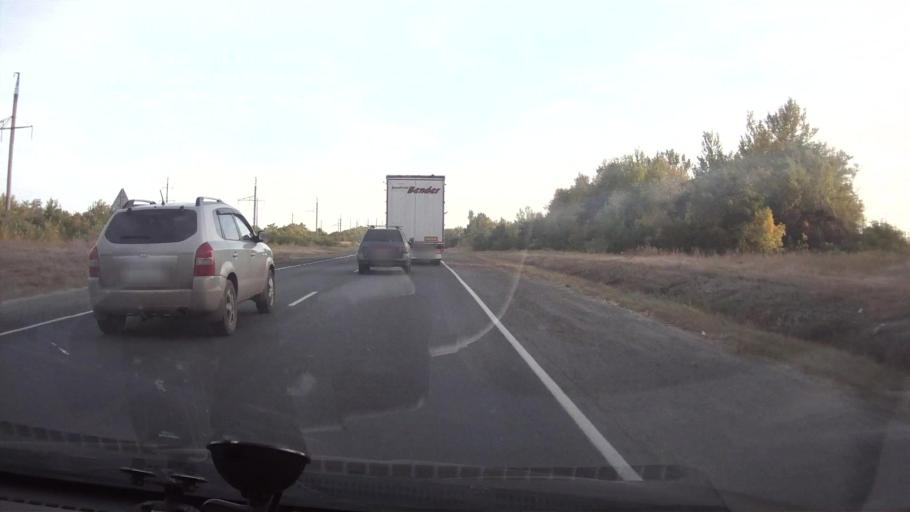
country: RU
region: Saratov
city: Krasnoarmeysk
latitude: 51.1621
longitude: 45.6491
